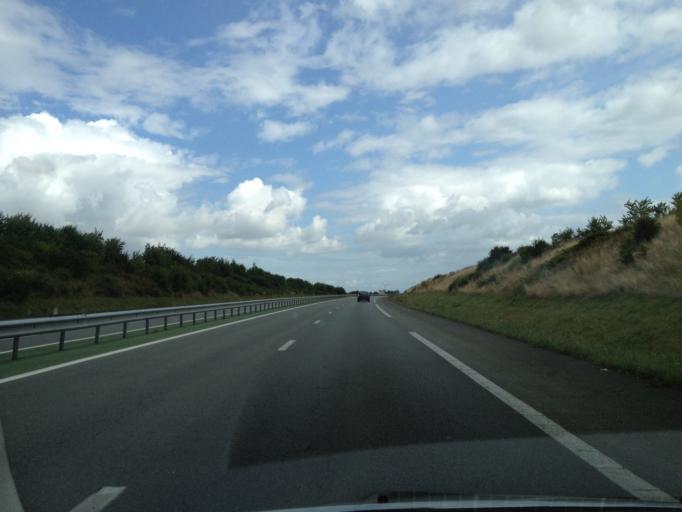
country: FR
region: Pays de la Loire
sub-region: Departement de Maine-et-Loire
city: Trementines
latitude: 47.1570
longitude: -0.8166
